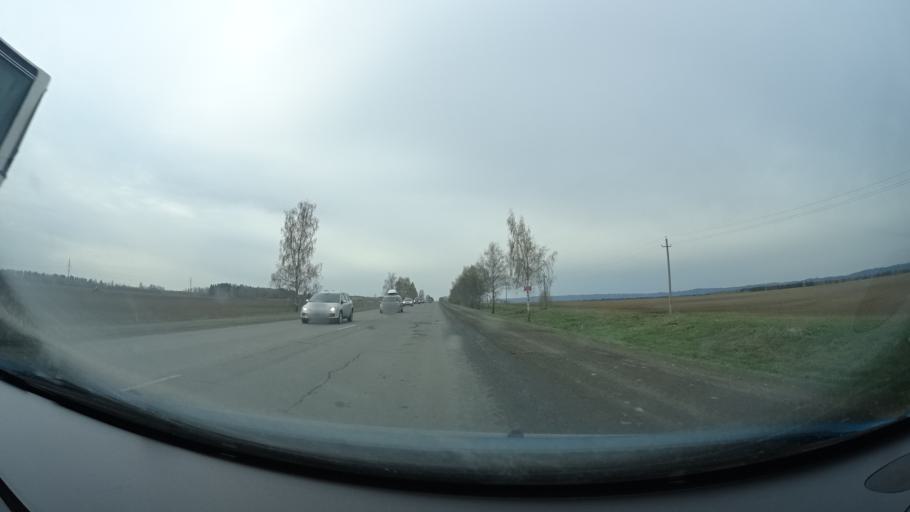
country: RU
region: Perm
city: Ust'-Kachka
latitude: 58.0622
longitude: 55.6158
